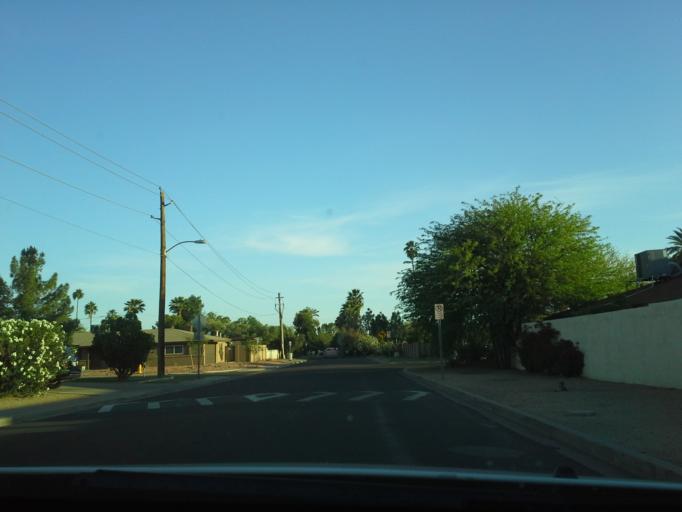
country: US
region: Arizona
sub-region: Maricopa County
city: Phoenix
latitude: 33.5410
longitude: -112.0607
